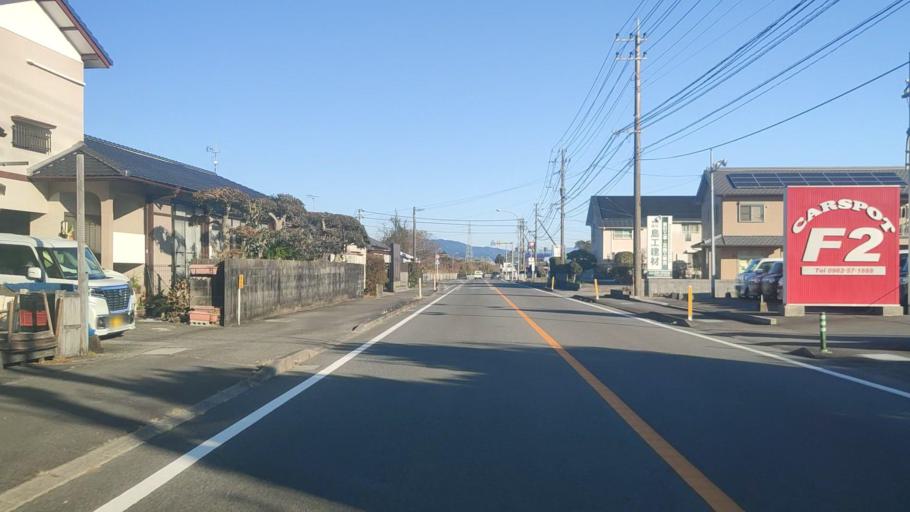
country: JP
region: Miyazaki
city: Nobeoka
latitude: 32.3869
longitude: 131.6275
